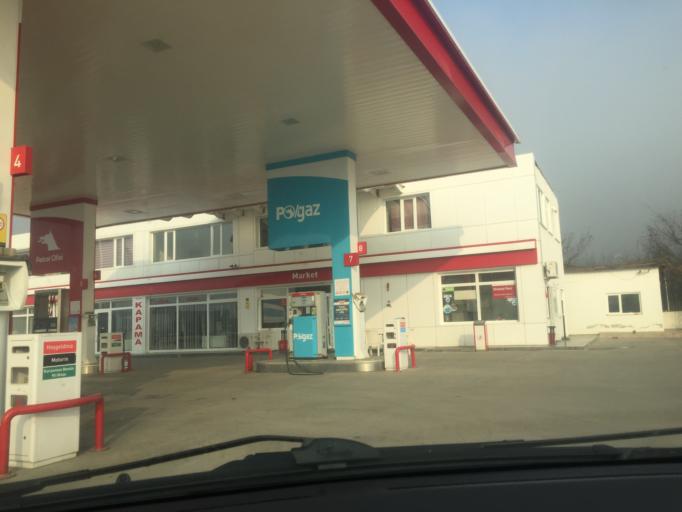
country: TR
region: Canakkale
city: Can
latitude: 40.0379
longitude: 27.0761
